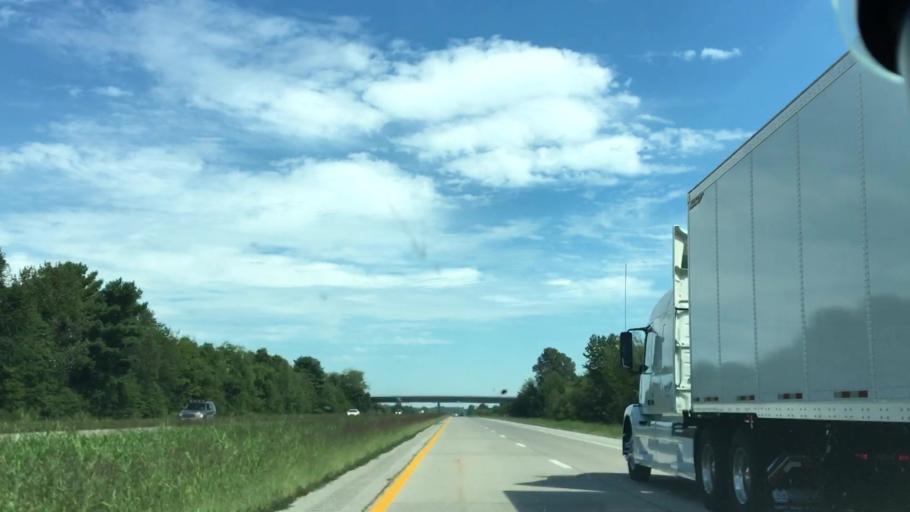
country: US
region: Kentucky
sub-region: Daviess County
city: Owensboro
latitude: 37.7620
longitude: -87.2347
